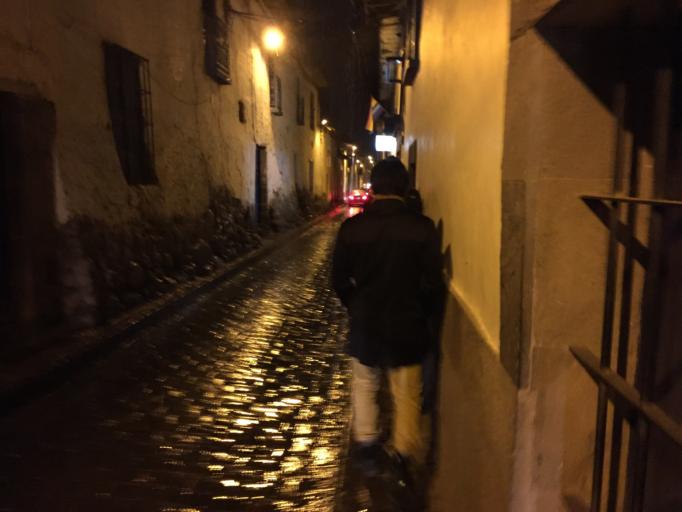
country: PE
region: Cusco
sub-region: Provincia de Cusco
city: Cusco
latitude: -13.5168
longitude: -71.9740
